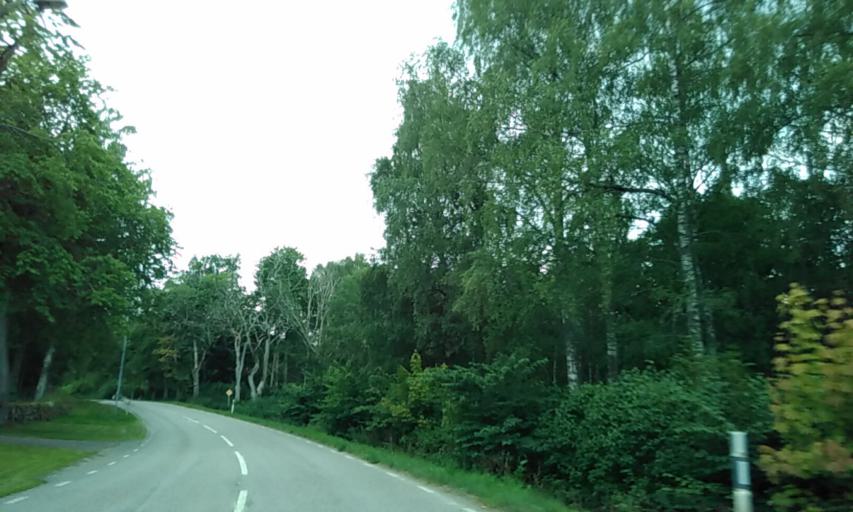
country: SE
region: Vaestra Goetaland
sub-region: Grastorps Kommun
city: Graestorp
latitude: 58.4756
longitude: 12.8282
